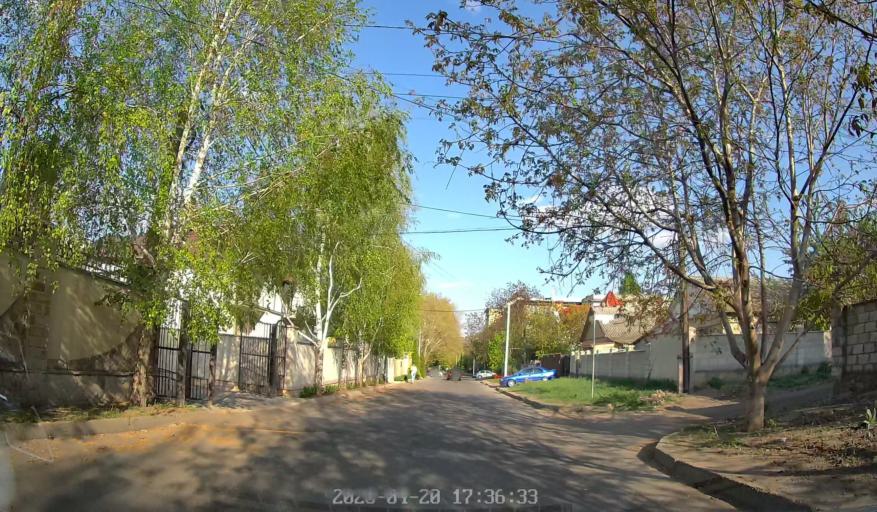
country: MD
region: Chisinau
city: Chisinau
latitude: 46.9888
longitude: 28.8635
